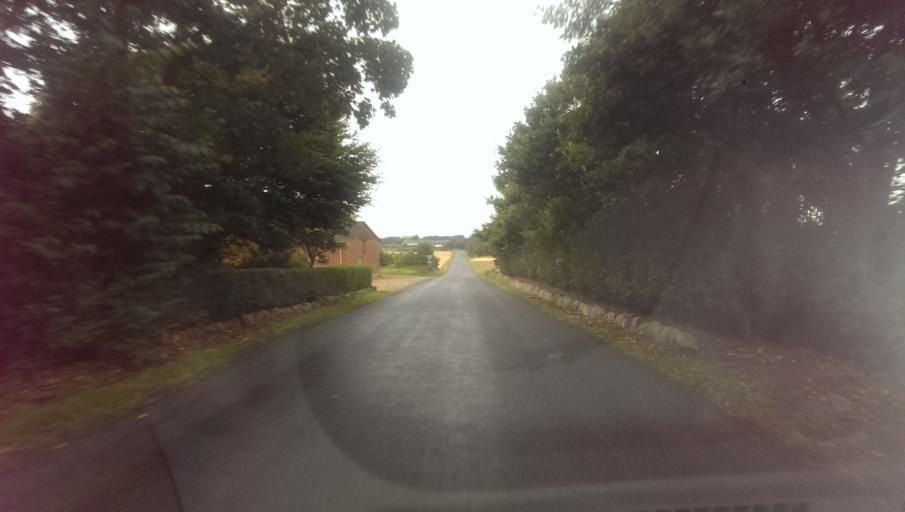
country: DK
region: South Denmark
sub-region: Esbjerg Kommune
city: Esbjerg
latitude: 55.5194
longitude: 8.4954
